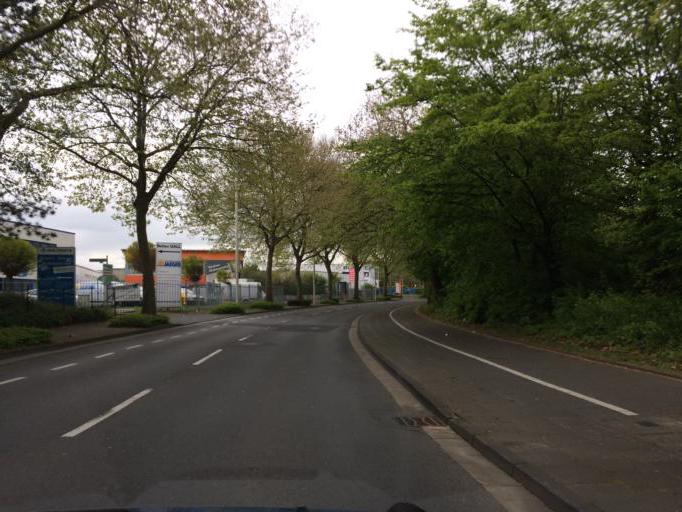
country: DE
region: North Rhine-Westphalia
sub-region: Regierungsbezirk Koln
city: Konigswinter
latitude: 50.6687
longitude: 7.1748
